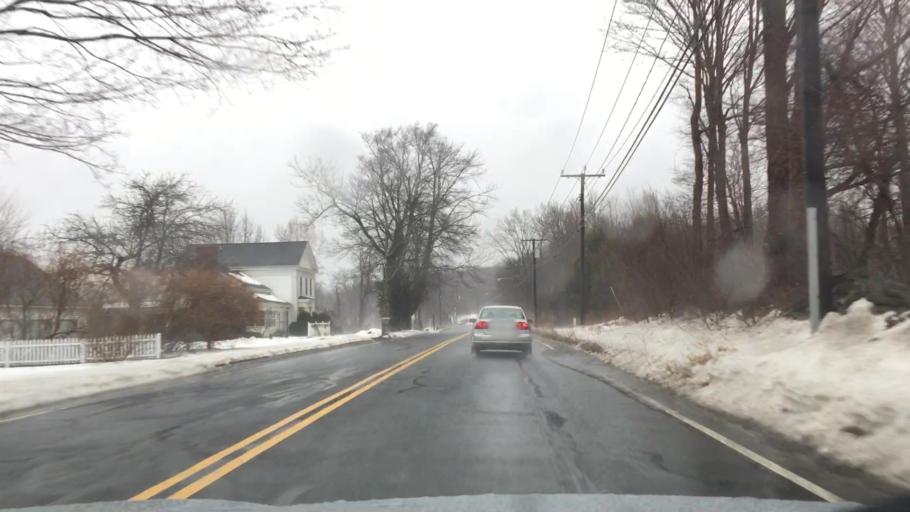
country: US
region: Massachusetts
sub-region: Hampden County
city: Ludlow
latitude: 42.1931
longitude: -72.4991
